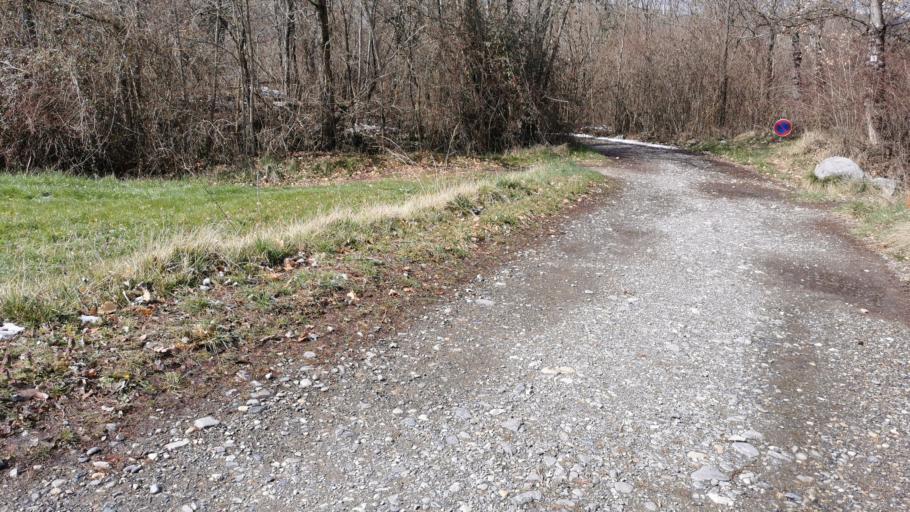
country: FR
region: Provence-Alpes-Cote d'Azur
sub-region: Departement des Alpes-de-Haute-Provence
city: Mallemoisson
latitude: 44.0621
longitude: 6.1757
